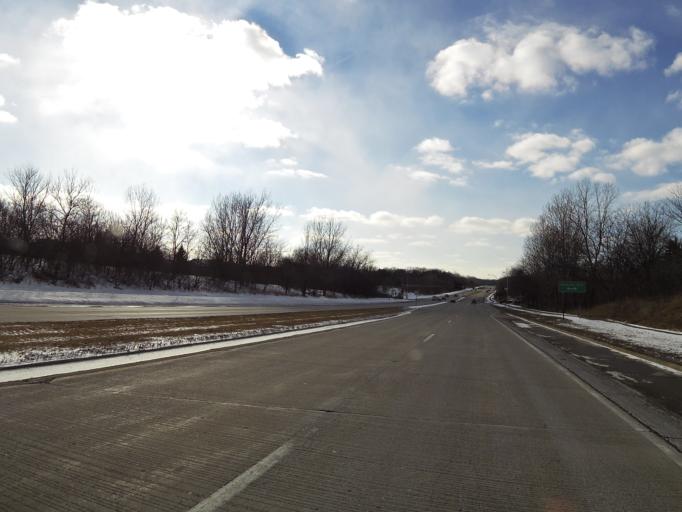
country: US
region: Minnesota
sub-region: Dakota County
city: Apple Valley
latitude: 44.7600
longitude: -93.2046
